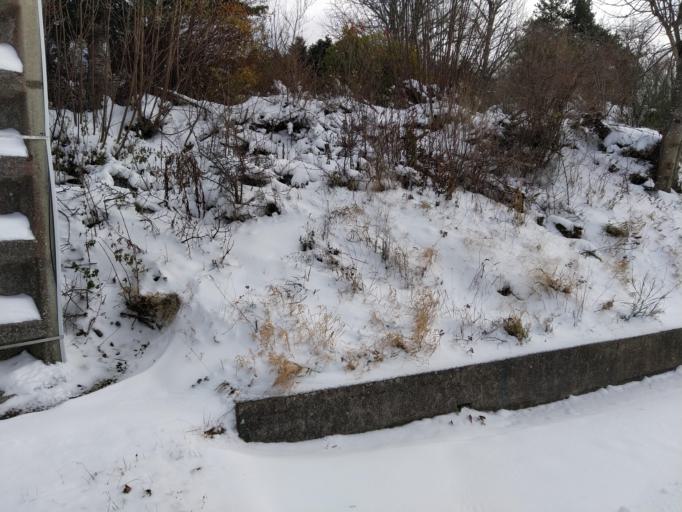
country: FR
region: Rhone-Alpes
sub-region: Departement de l'Ardeche
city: Saint-Agreve
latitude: 44.9680
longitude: 4.4110
